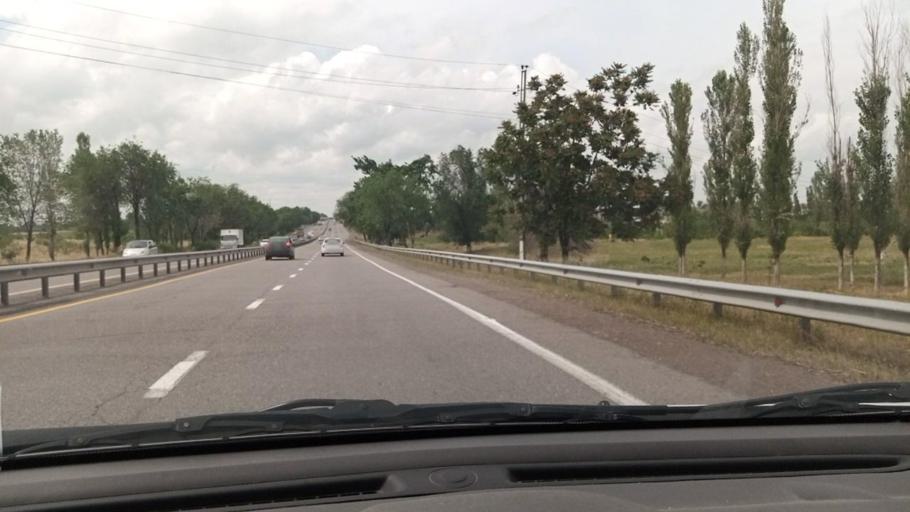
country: UZ
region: Toshkent
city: Tuytepa
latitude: 41.0213
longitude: 69.5120
